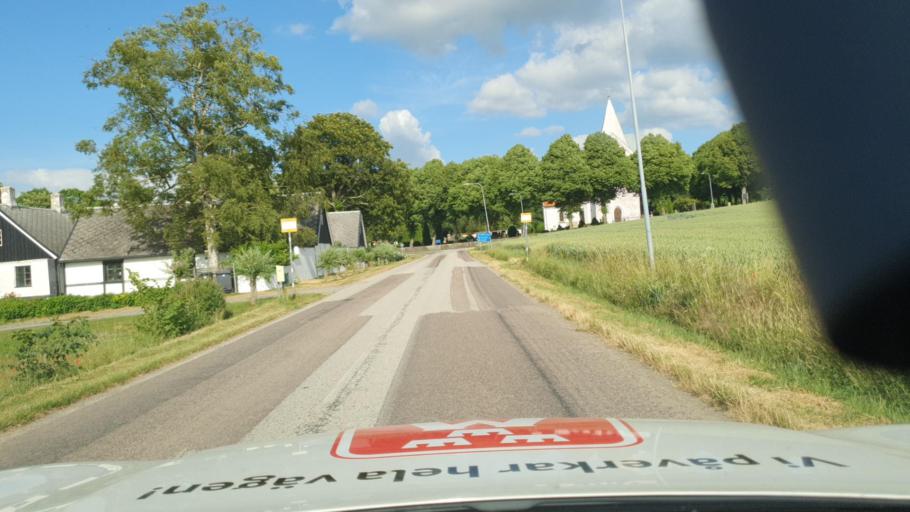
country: SE
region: Skane
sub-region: Skurups Kommun
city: Rydsgard
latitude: 55.4353
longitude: 13.6142
